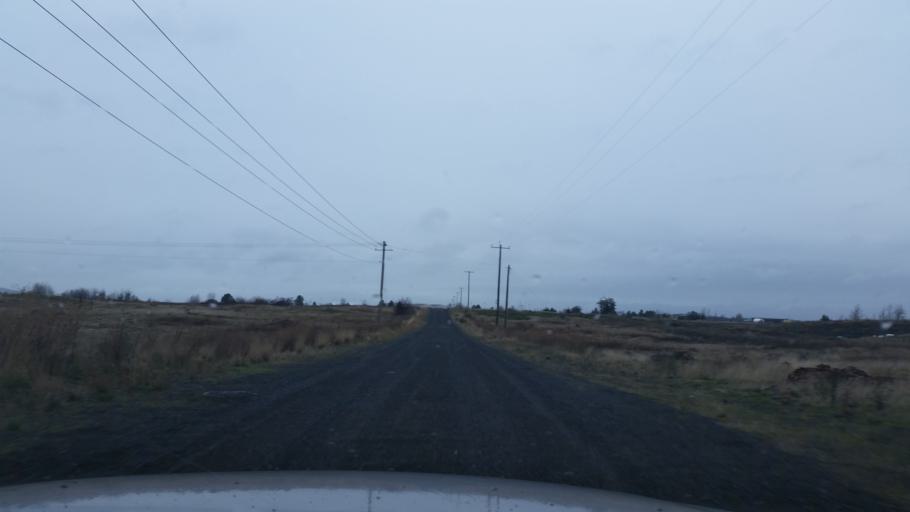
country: US
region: Washington
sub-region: Spokane County
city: Airway Heights
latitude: 47.6284
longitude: -117.6066
